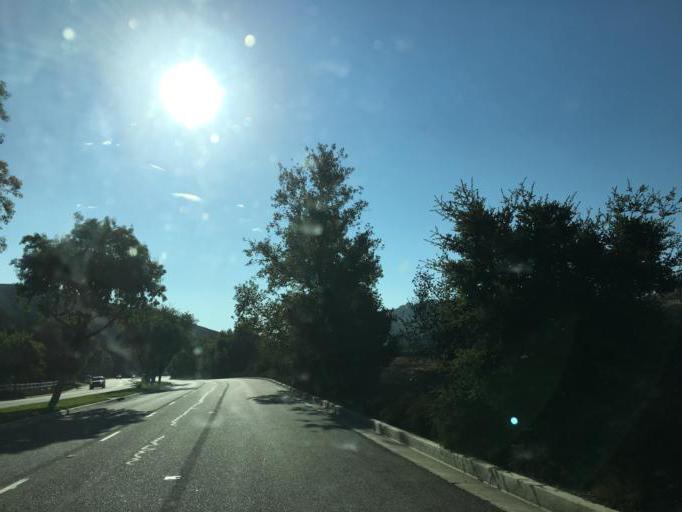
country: US
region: California
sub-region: Los Angeles County
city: Hidden Hills
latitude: 34.1521
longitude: -118.6829
